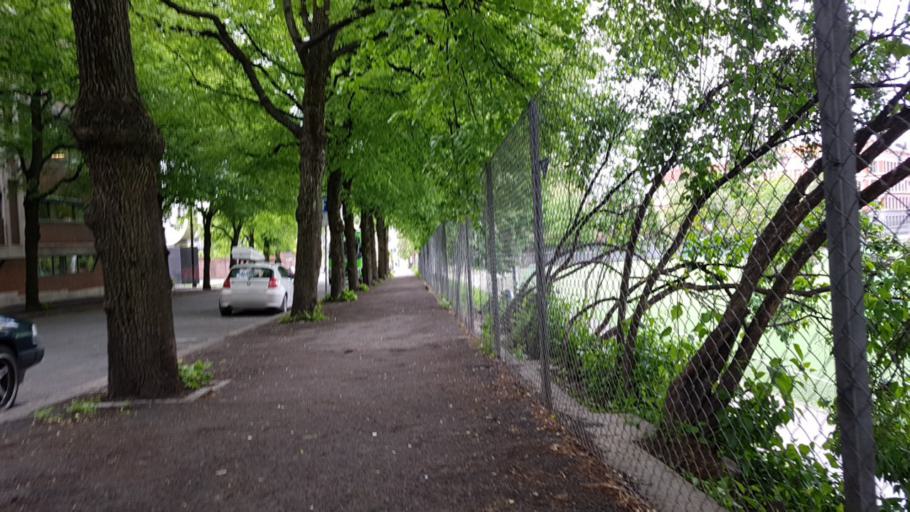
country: NO
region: Oslo
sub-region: Oslo
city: Oslo
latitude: 59.9264
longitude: 10.7657
